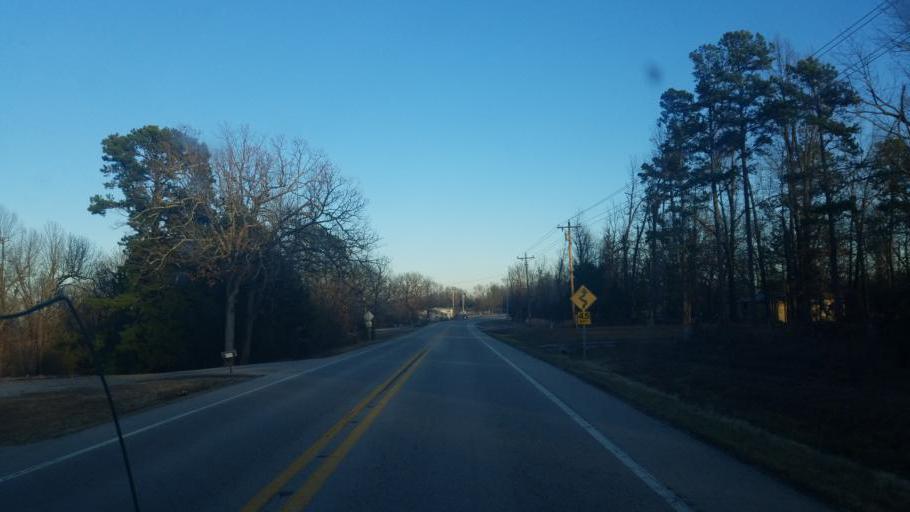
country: US
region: Arkansas
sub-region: Baxter County
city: Mountain Home
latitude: 36.3847
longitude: -92.1640
